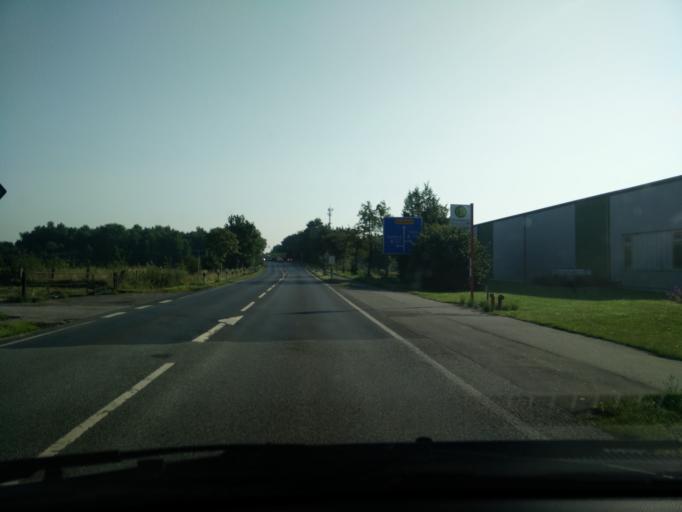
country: DE
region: Schleswig-Holstein
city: Ellerhoop
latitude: 53.7146
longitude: 9.7514
